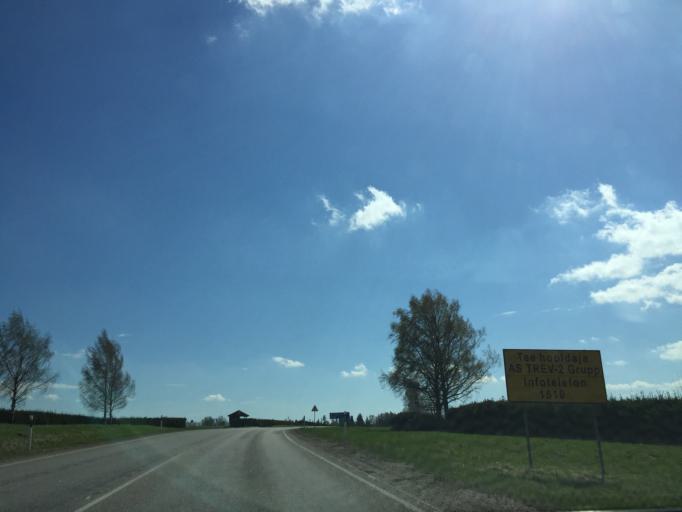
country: EE
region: Tartu
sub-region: Elva linn
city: Elva
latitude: 58.1121
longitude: 26.2399
